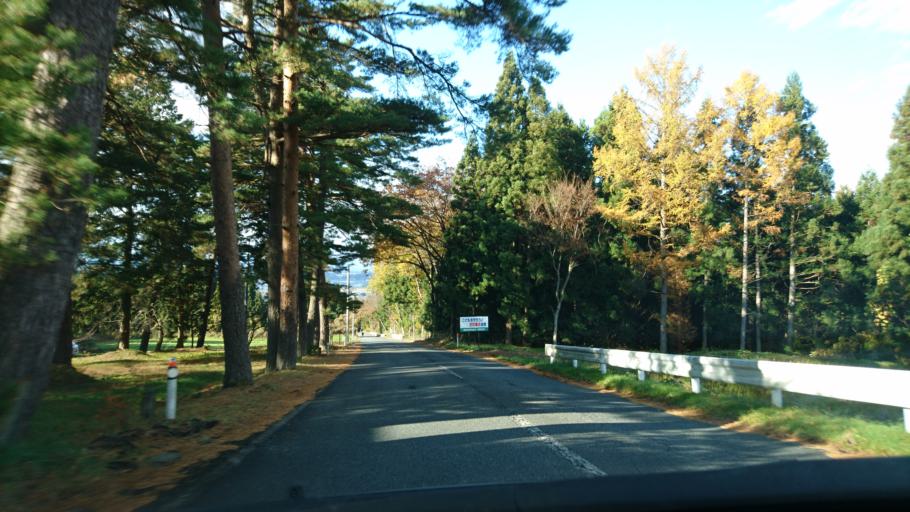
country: JP
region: Iwate
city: Mizusawa
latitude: 39.0302
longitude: 141.1626
